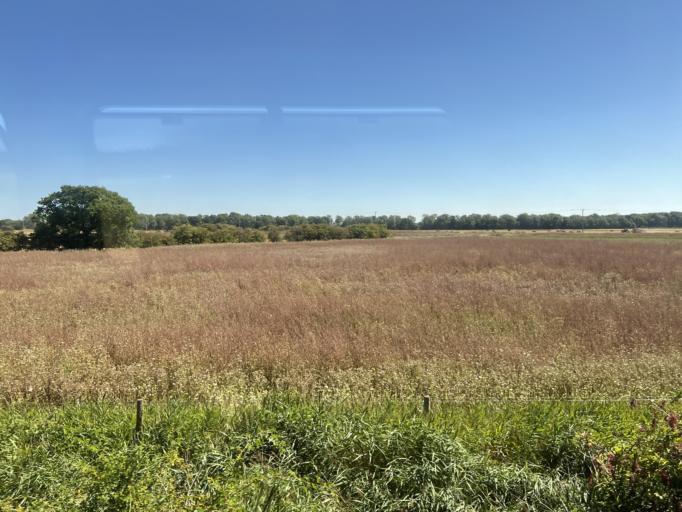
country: GB
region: England
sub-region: Lincolnshire
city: Spilsby
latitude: 53.1139
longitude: 0.1282
